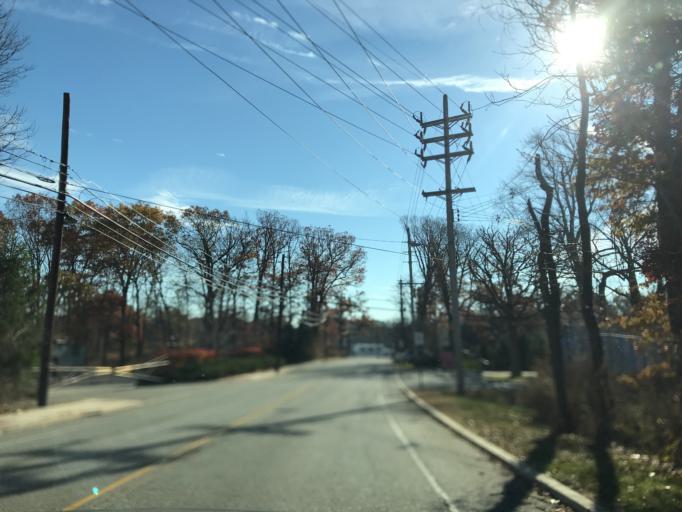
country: US
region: New Jersey
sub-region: Morris County
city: Boonton
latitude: 40.8960
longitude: -74.4171
